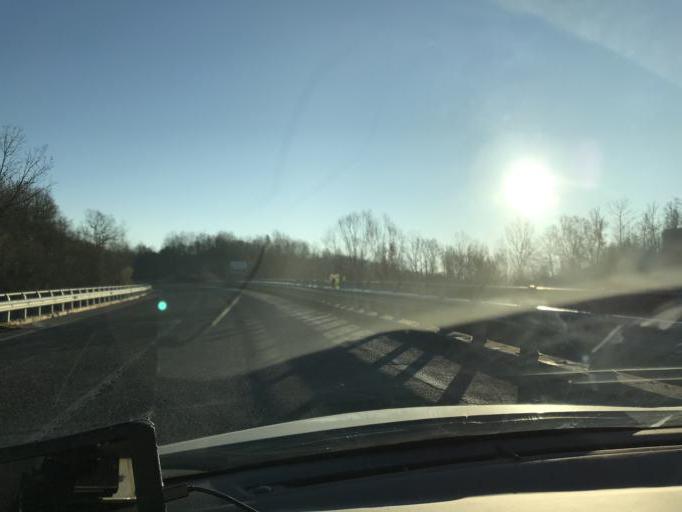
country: IT
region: Latium
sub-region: Provincia di Rieti
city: Fiamignano
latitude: 42.2611
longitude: 13.0951
